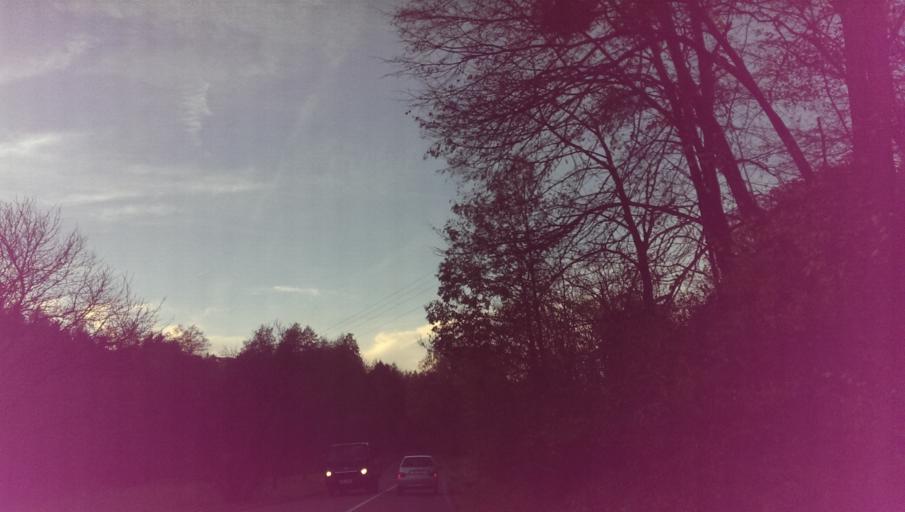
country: CZ
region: Zlin
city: Tecovice
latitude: 49.1948
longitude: 17.6024
